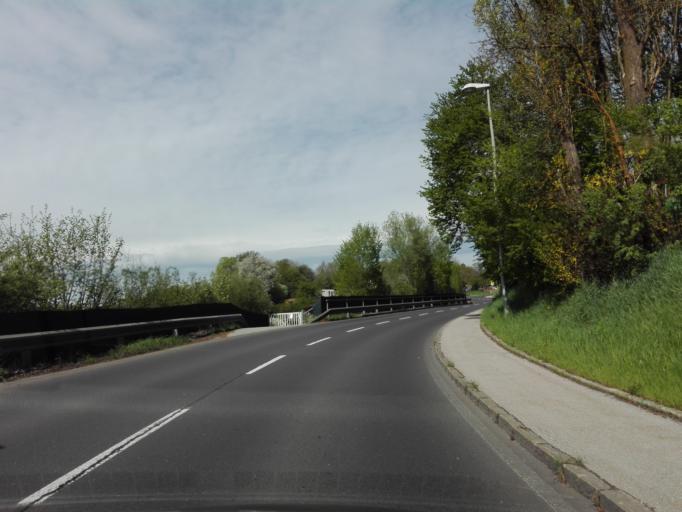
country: AT
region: Upper Austria
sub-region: Linz Stadt
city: Linz
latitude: 48.3090
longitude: 14.2668
